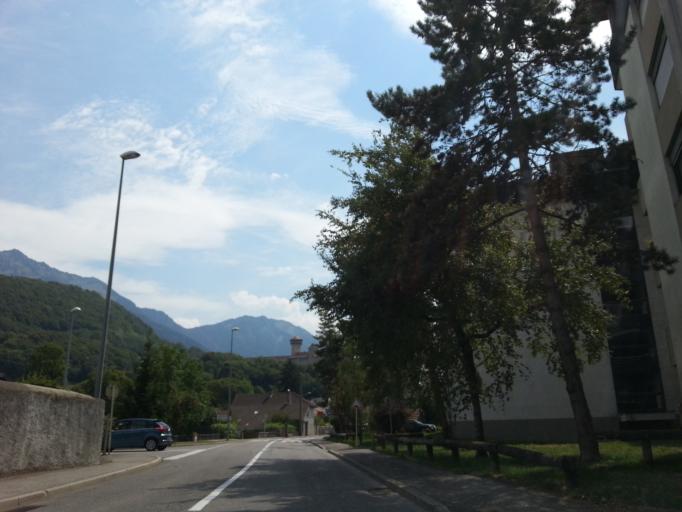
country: FR
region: Rhone-Alpes
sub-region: Departement de la Haute-Savoie
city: Faverges
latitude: 45.7496
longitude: 6.2950
